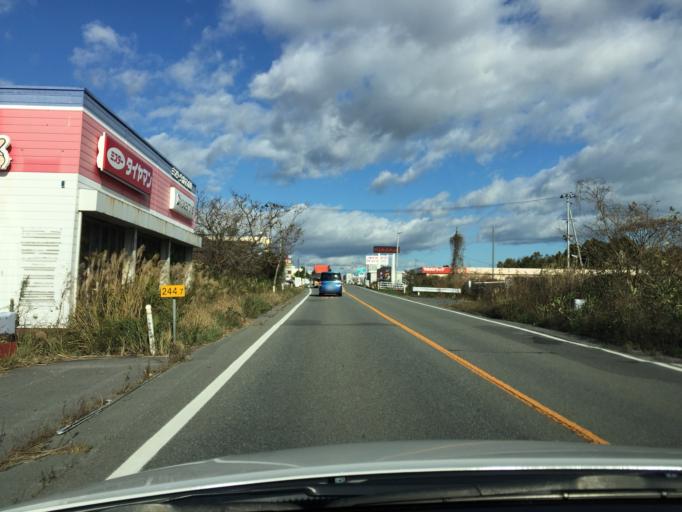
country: JP
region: Fukushima
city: Namie
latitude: 37.3552
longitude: 141.0106
